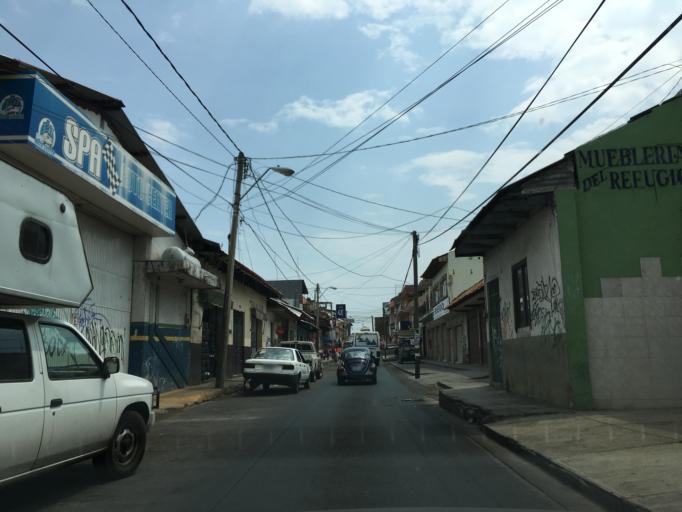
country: MX
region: Michoacan
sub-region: Uruapan
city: Uruapan
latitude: 19.4136
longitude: -102.0651
